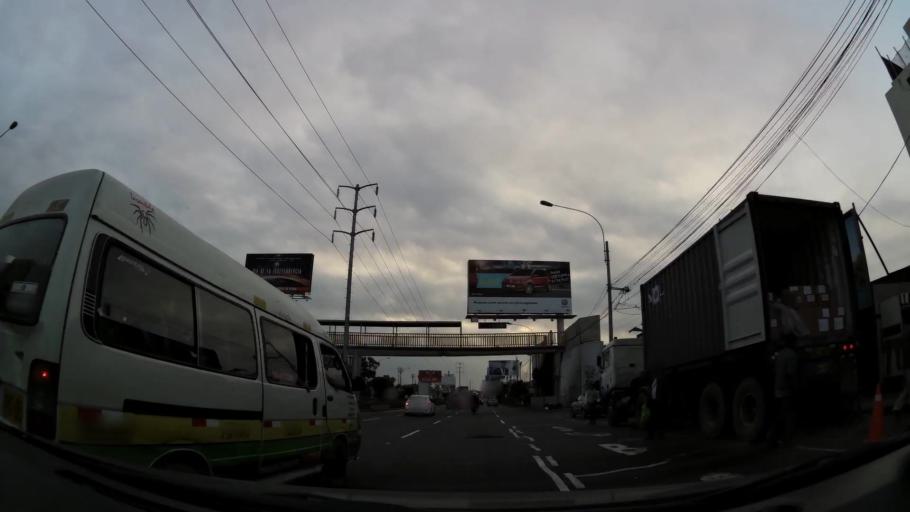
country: PE
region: Lima
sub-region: Lima
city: San Isidro
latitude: -12.0806
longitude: -77.0729
